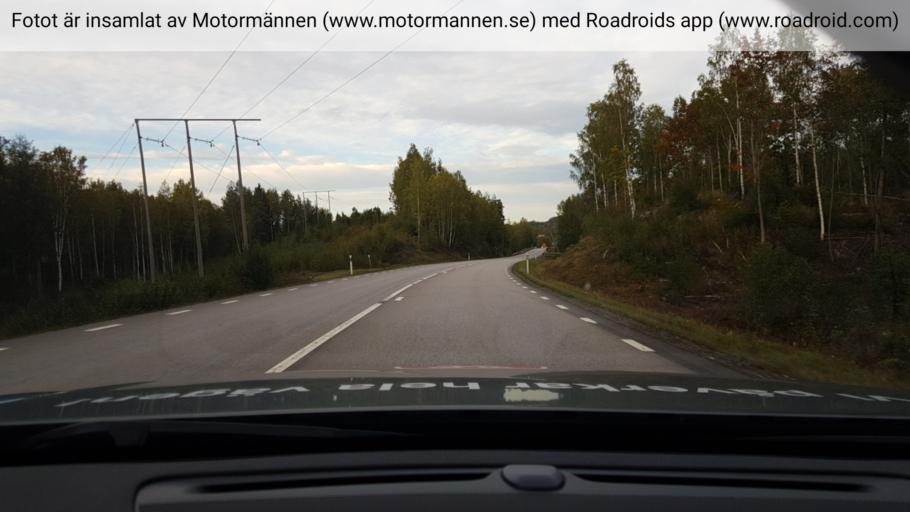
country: SE
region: Vaestra Goetaland
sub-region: Bengtsfors Kommun
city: Bengtsfors
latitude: 59.0206
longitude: 12.2716
